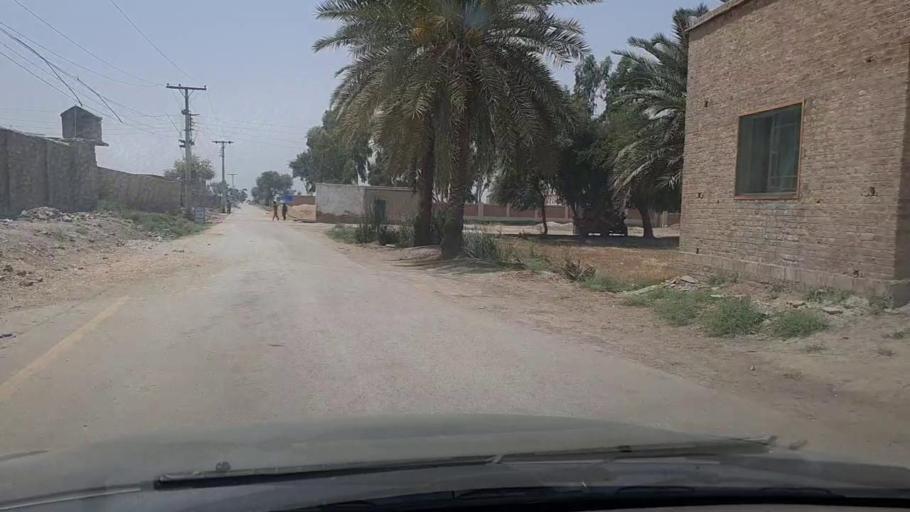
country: PK
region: Sindh
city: Miro Khan
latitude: 27.7730
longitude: 68.1610
